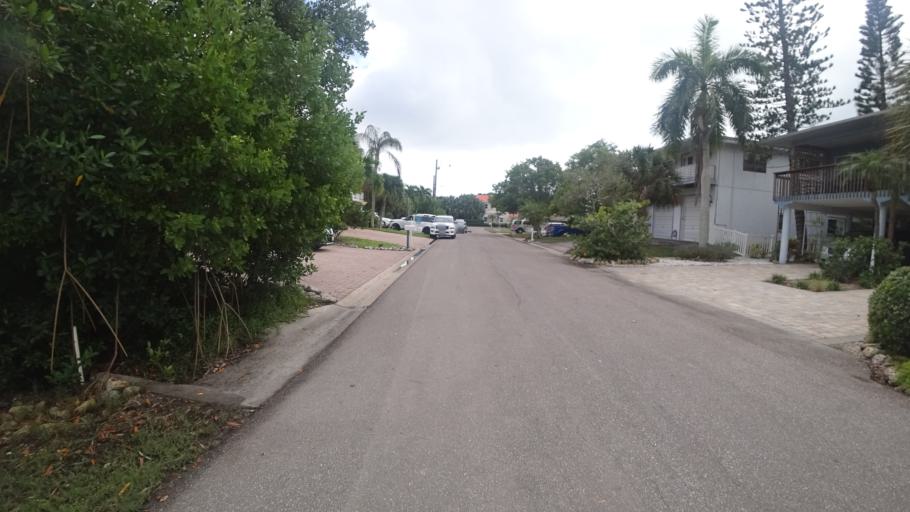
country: US
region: Florida
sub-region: Manatee County
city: Bradenton Beach
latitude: 27.4817
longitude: -82.7022
